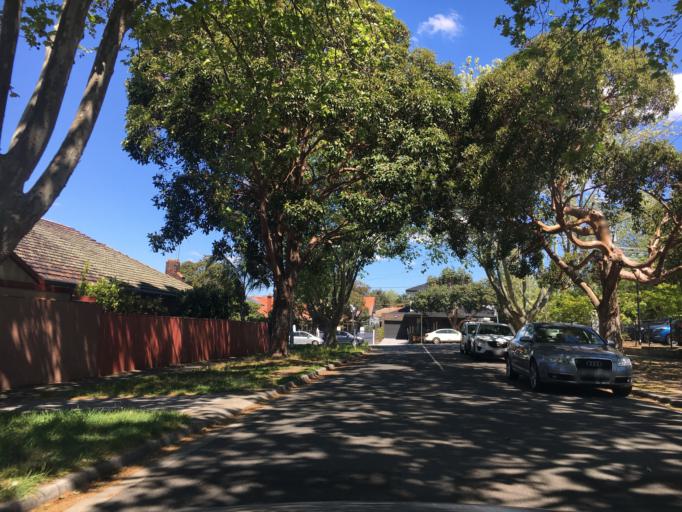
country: AU
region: Victoria
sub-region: Monash
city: Chadstone
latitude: -37.8995
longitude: 145.0992
